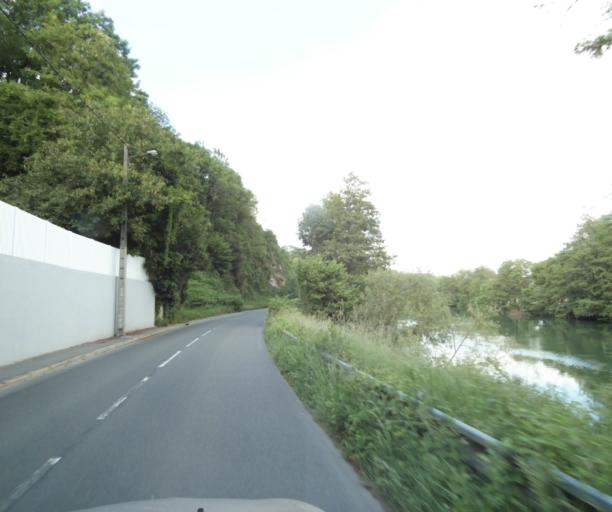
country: FR
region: Champagne-Ardenne
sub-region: Departement des Ardennes
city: Charleville-Mezieres
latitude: 49.7830
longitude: 4.7176
